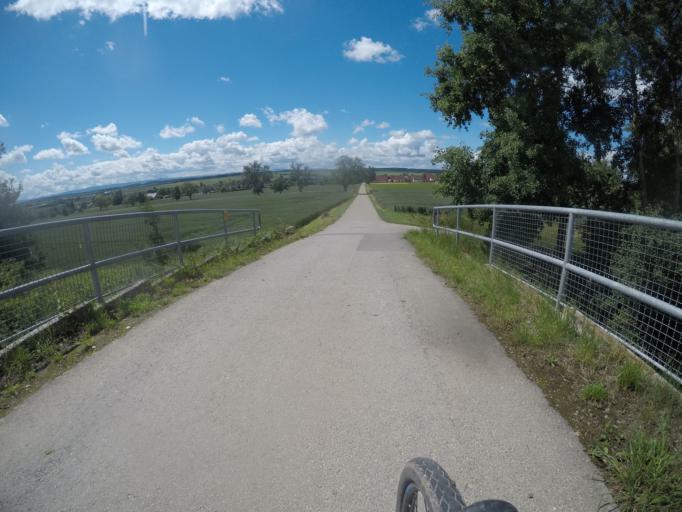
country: DE
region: Baden-Wuerttemberg
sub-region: Regierungsbezirk Stuttgart
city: Motzingen
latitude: 48.4851
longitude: 8.7497
